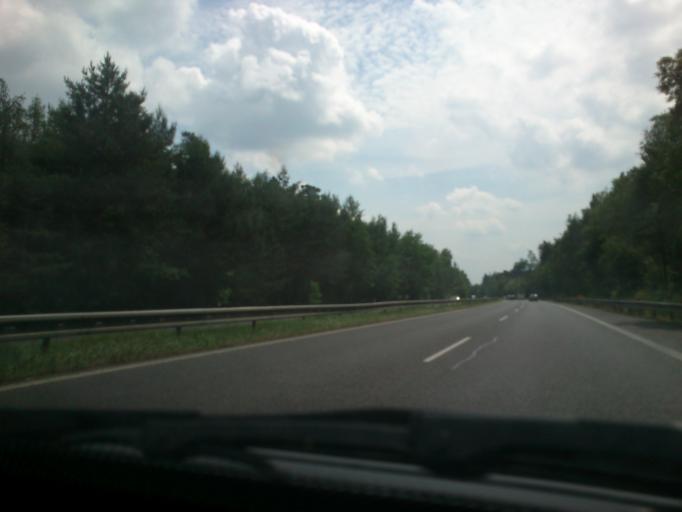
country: CZ
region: Central Bohemia
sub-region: Okres Mlada Boleslav
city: Mlada Boleslav
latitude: 50.3541
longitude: 14.8719
